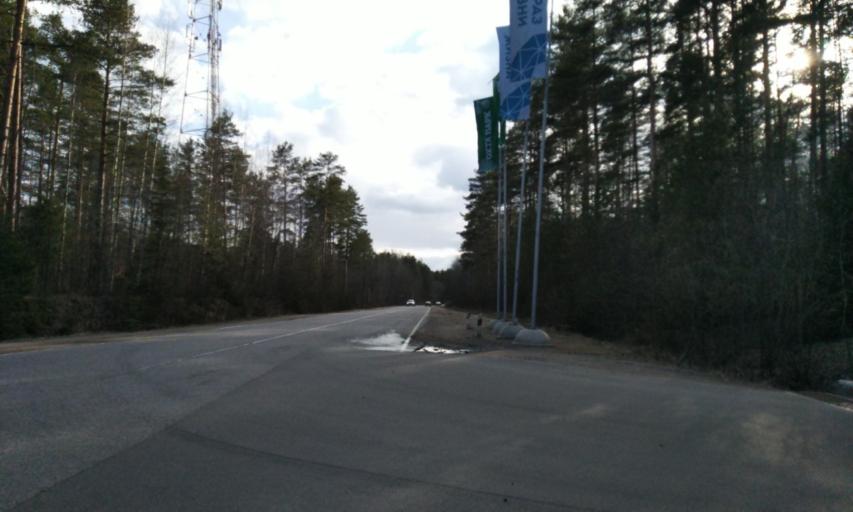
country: RU
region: Leningrad
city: Toksovo
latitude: 60.1271
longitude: 30.4640
